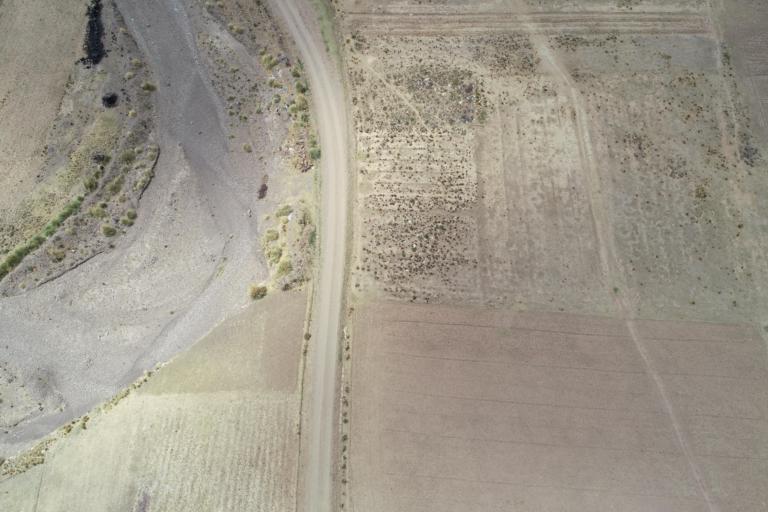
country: BO
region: La Paz
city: Achacachi
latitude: -15.9143
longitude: -68.8847
